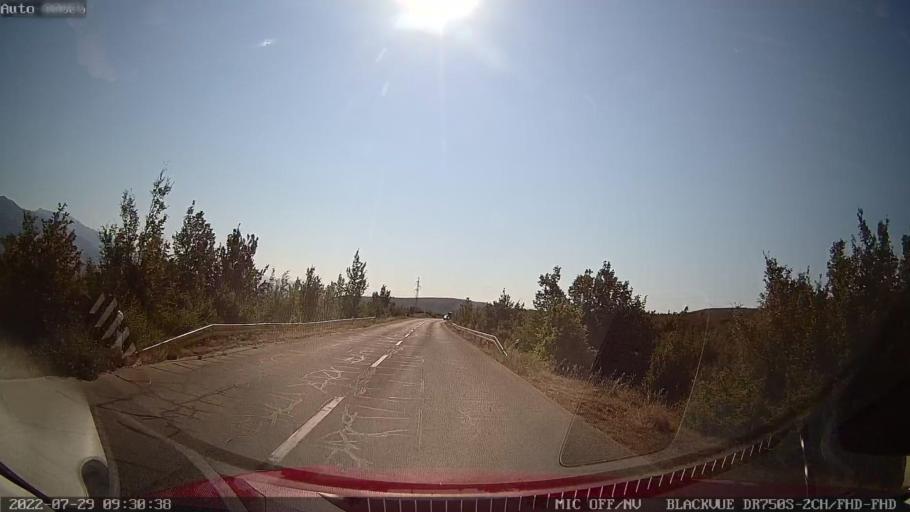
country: HR
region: Zadarska
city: Obrovac
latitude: 44.1932
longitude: 15.6885
